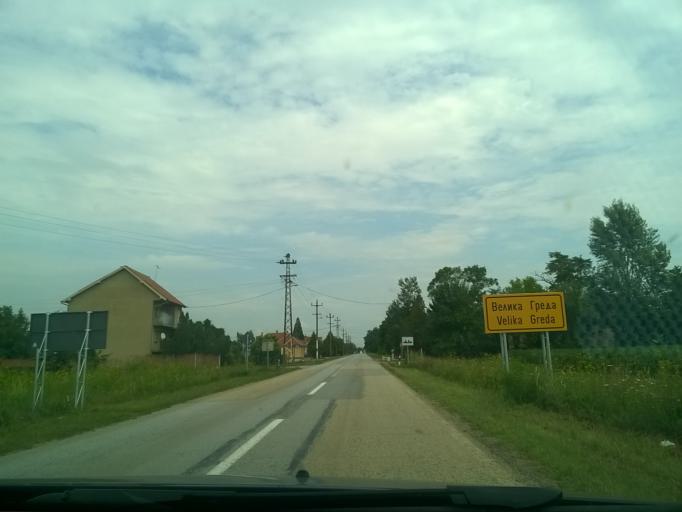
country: RS
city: Velika Greda
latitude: 45.2356
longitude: 21.0187
